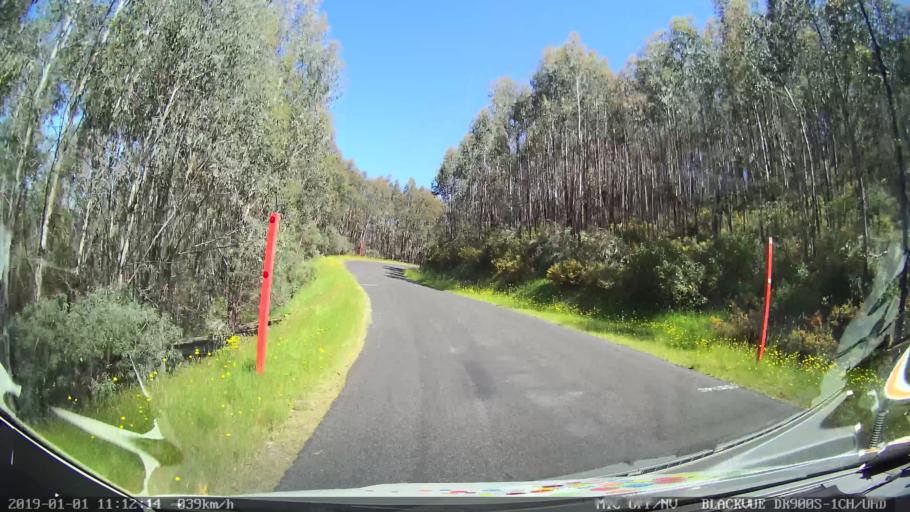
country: AU
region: New South Wales
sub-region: Snowy River
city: Jindabyne
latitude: -35.9577
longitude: 148.4005
